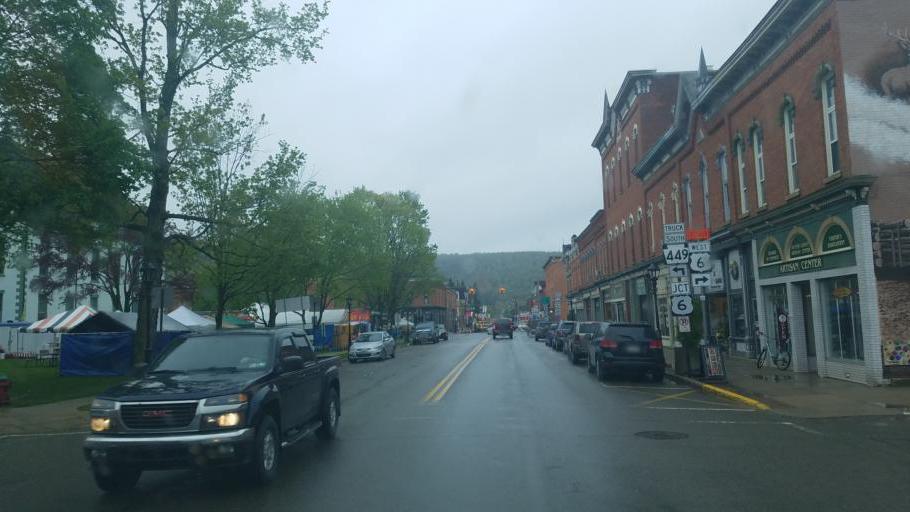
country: US
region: Pennsylvania
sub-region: Potter County
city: Coudersport
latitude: 41.7756
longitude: -78.0209
